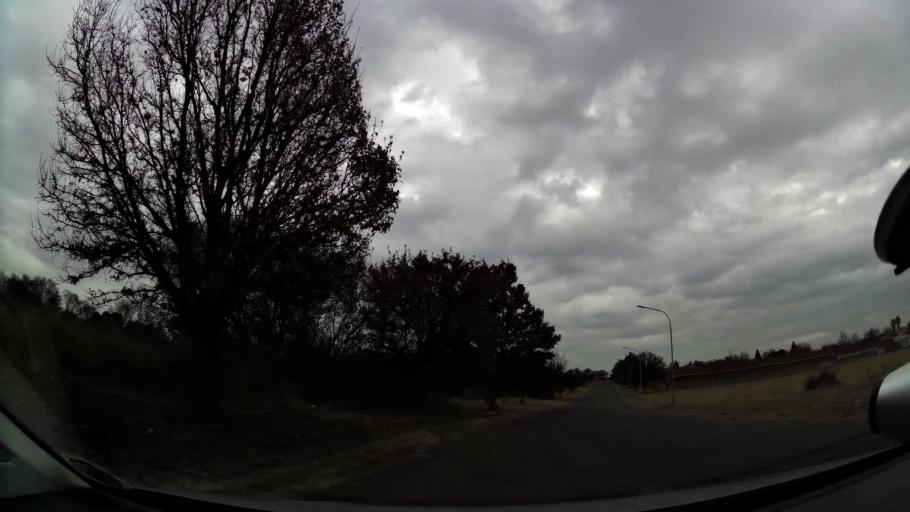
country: ZA
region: Orange Free State
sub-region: Fezile Dabi District Municipality
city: Kroonstad
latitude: -27.6513
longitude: 27.2438
